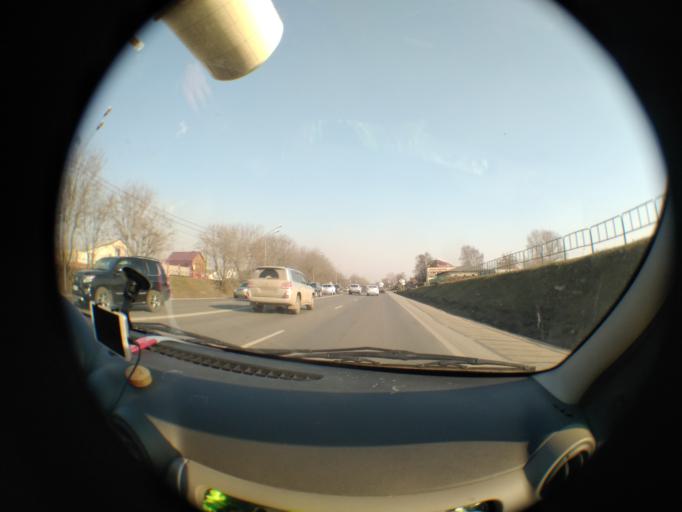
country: RU
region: Moskovskaya
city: Ostrovtsy
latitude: 55.5953
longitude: 37.9924
